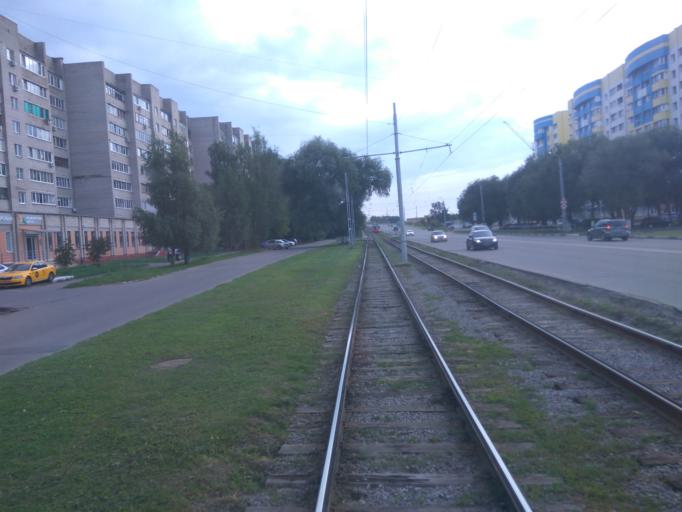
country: RU
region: Moskovskaya
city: Kolomna
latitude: 55.0758
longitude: 38.7613
